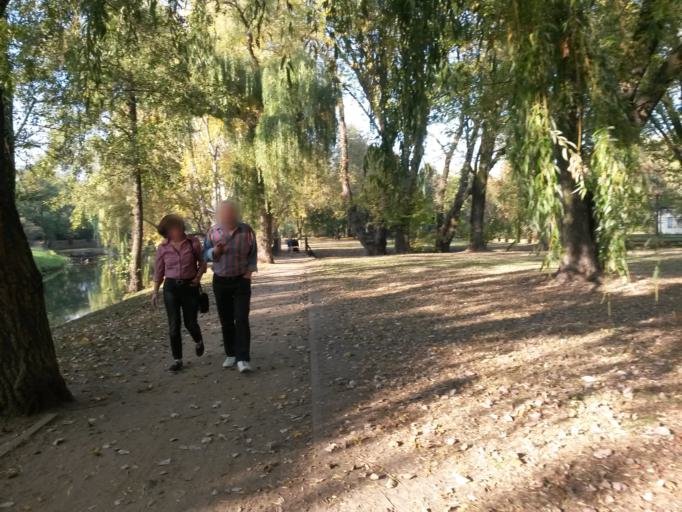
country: PL
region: Masovian Voivodeship
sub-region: Warszawa
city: Mokotow
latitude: 52.1995
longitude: 21.0407
